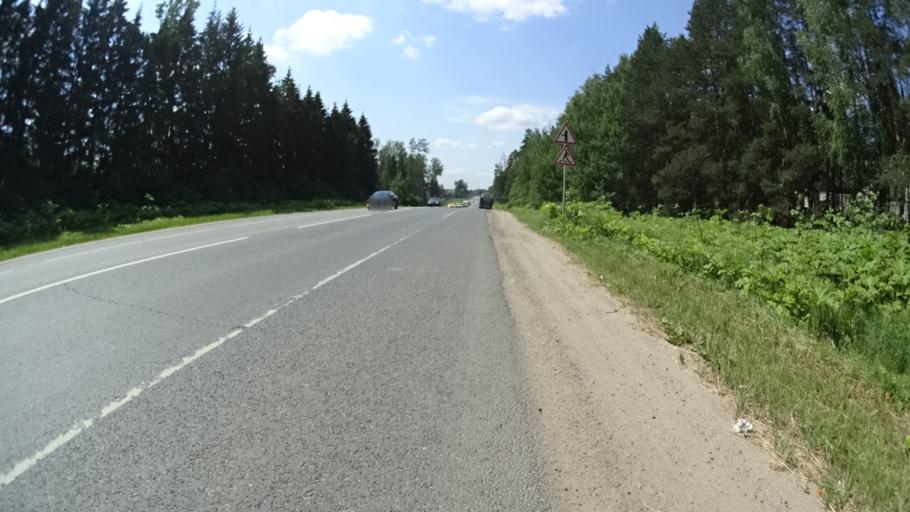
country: RU
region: Moskovskaya
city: Lesnoy
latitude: 56.0588
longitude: 38.0069
